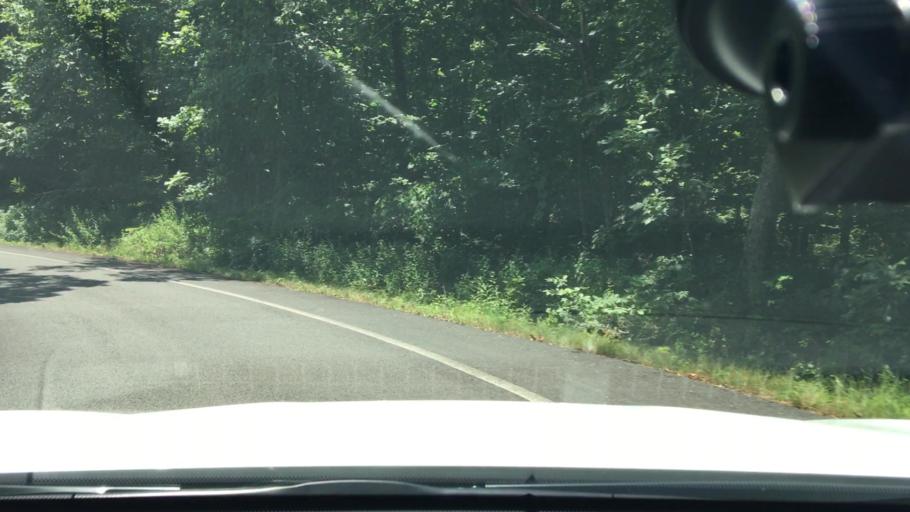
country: US
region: Arkansas
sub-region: Logan County
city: Paris
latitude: 35.1736
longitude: -93.6416
